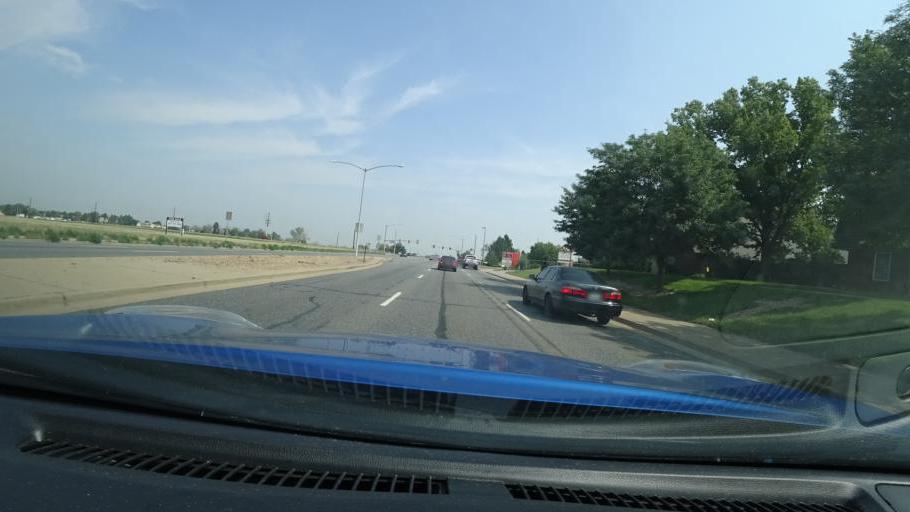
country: US
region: Colorado
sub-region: Adams County
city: Aurora
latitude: 39.7387
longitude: -104.7912
